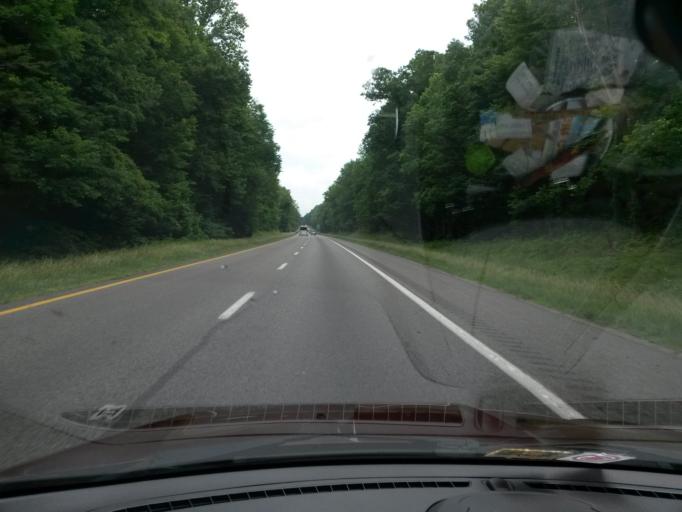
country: US
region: Virginia
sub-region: Goochland County
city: Goochland
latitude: 37.7171
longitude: -77.8070
